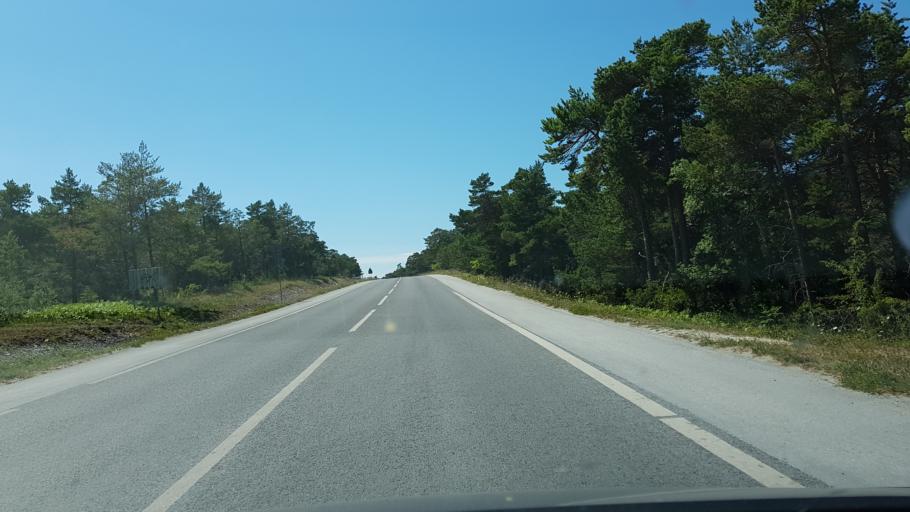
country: SE
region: Gotland
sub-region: Gotland
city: Visby
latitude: 57.6855
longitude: 18.3551
